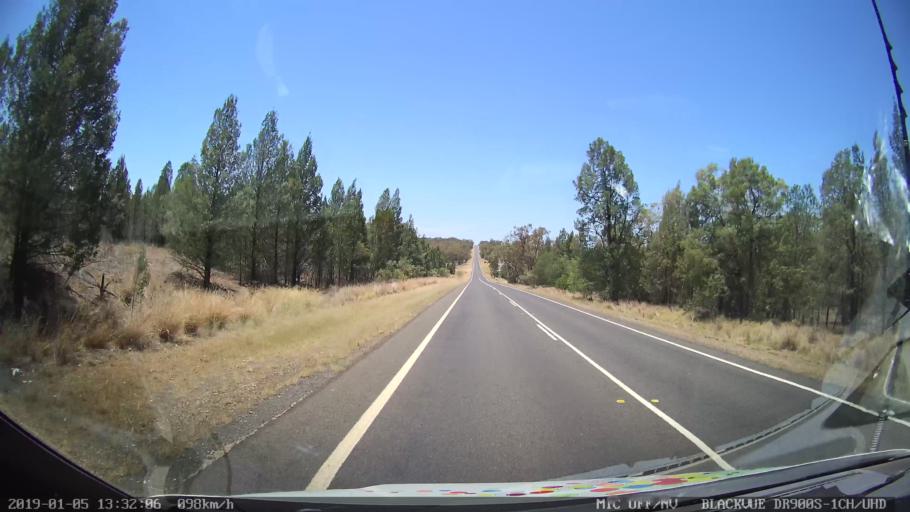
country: AU
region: New South Wales
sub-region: Gunnedah
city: Gunnedah
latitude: -31.0074
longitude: 150.0947
